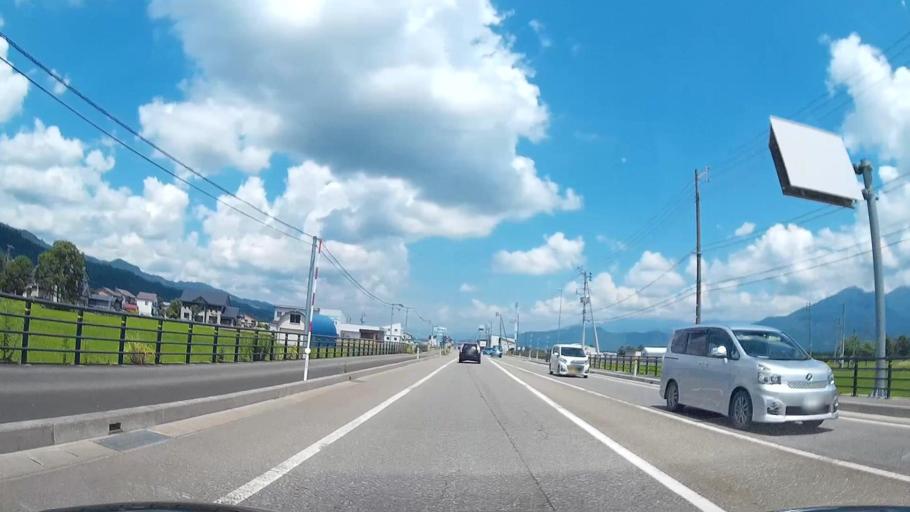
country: JP
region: Niigata
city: Shiozawa
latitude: 37.0041
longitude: 138.8175
